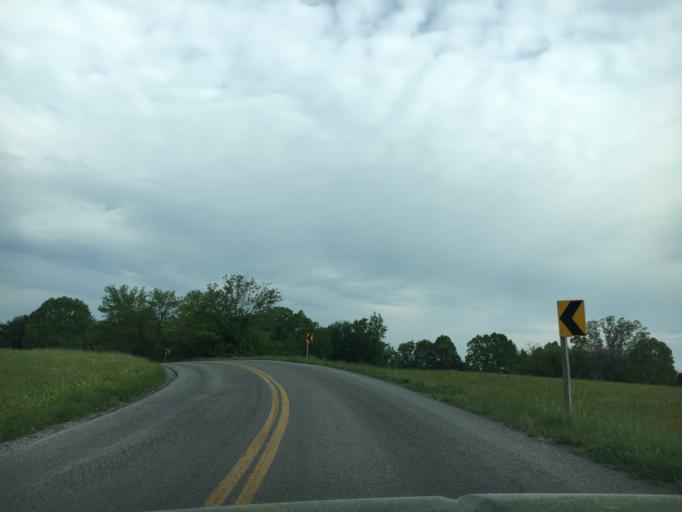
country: US
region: Virginia
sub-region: Campbell County
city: Brookneal
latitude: 36.9095
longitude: -78.9156
